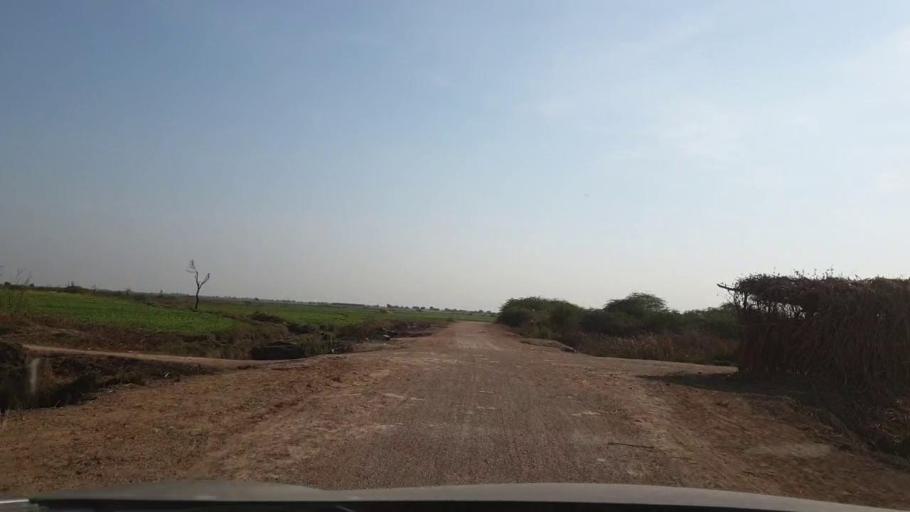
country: PK
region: Sindh
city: Berani
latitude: 25.7130
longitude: 68.8066
